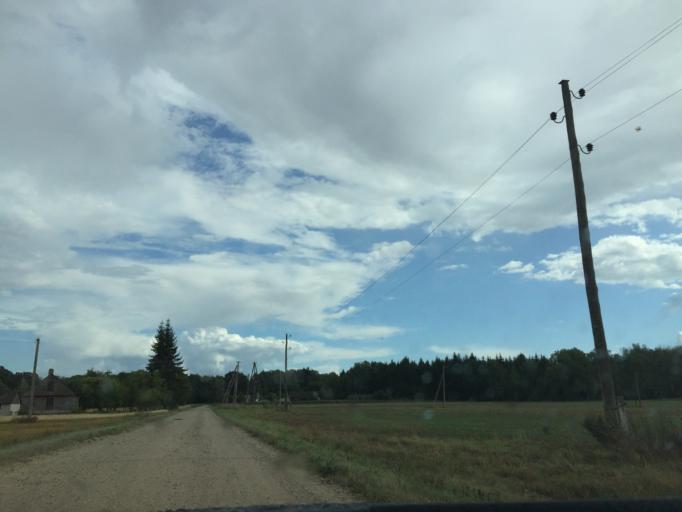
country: LT
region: Siauliu apskritis
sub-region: Joniskis
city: Joniskis
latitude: 56.3397
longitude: 23.5559
